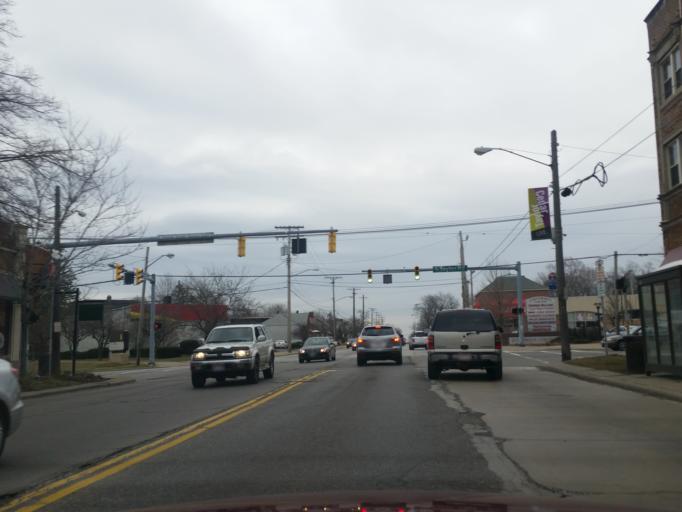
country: US
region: Ohio
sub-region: Cuyahoga County
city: Cleveland Heights
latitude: 41.5013
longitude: -81.5566
